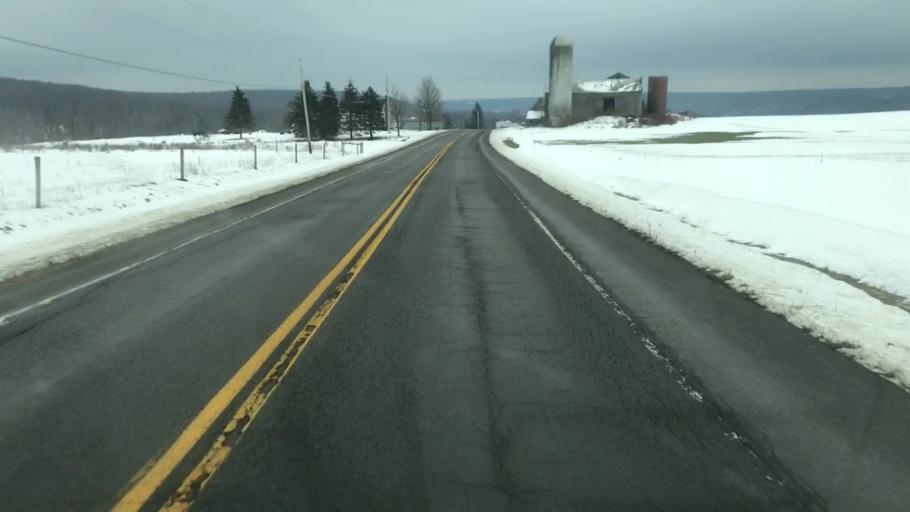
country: US
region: New York
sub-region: Cayuga County
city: Moravia
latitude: 42.7201
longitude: -76.3135
